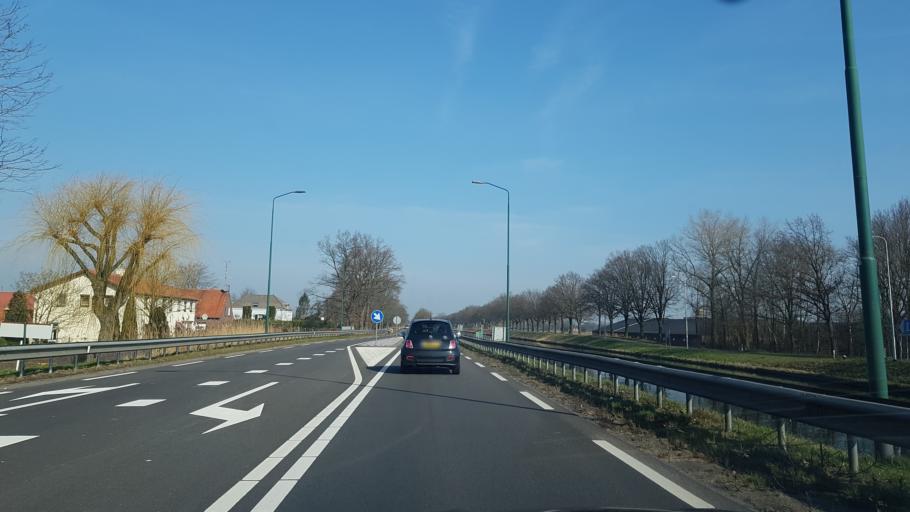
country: NL
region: Limburg
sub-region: Gemeente Nederweert
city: Nederweert
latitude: 51.3309
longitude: 5.7462
